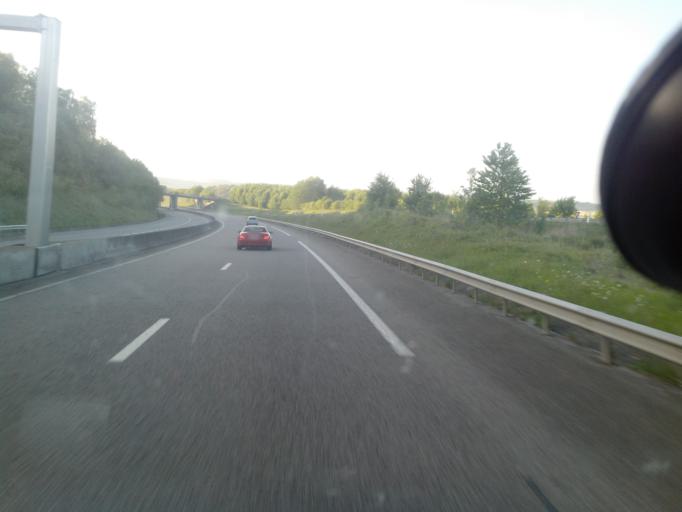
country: FR
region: Haute-Normandie
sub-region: Departement de la Seine-Maritime
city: Neufchatel-en-Bray
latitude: 49.7575
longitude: 1.4852
